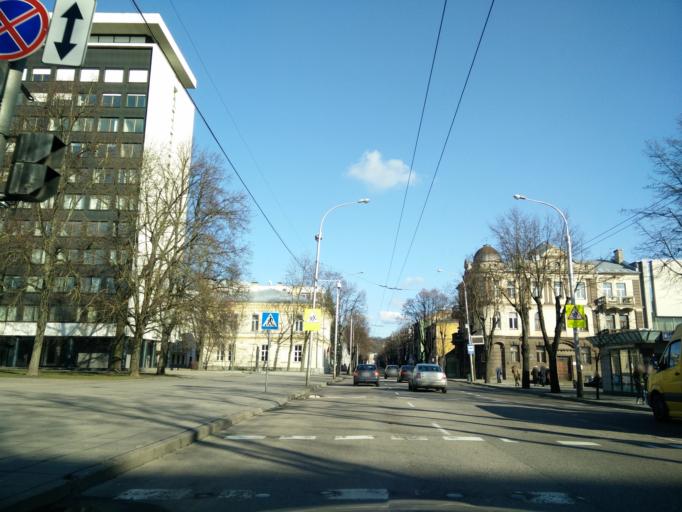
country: LT
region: Kauno apskritis
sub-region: Kaunas
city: Kaunas
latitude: 54.8991
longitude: 23.9134
